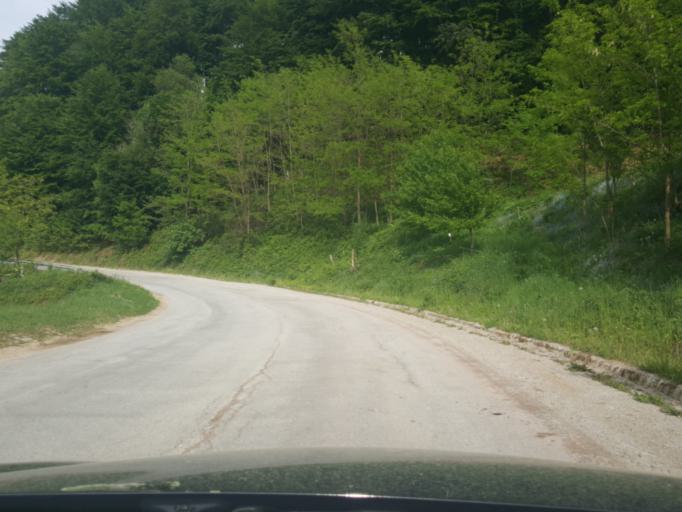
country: RS
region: Central Serbia
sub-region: Zlatiborski Okrug
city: Bajina Basta
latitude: 44.0710
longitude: 19.6568
